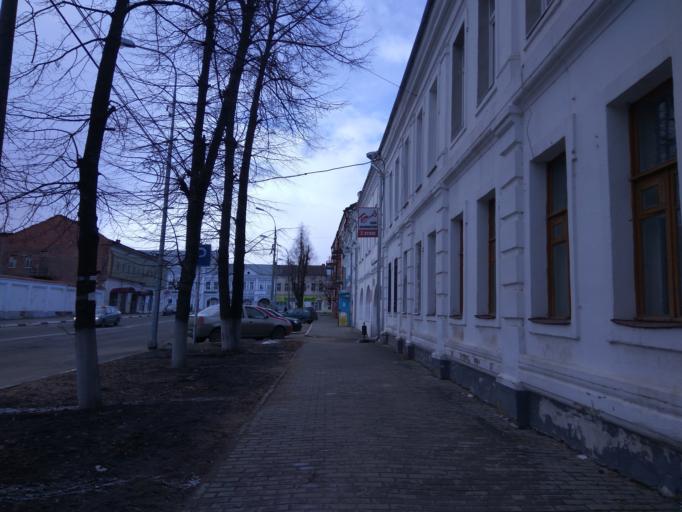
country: RU
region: Jaroslavl
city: Rostov
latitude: 57.1858
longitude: 39.4195
